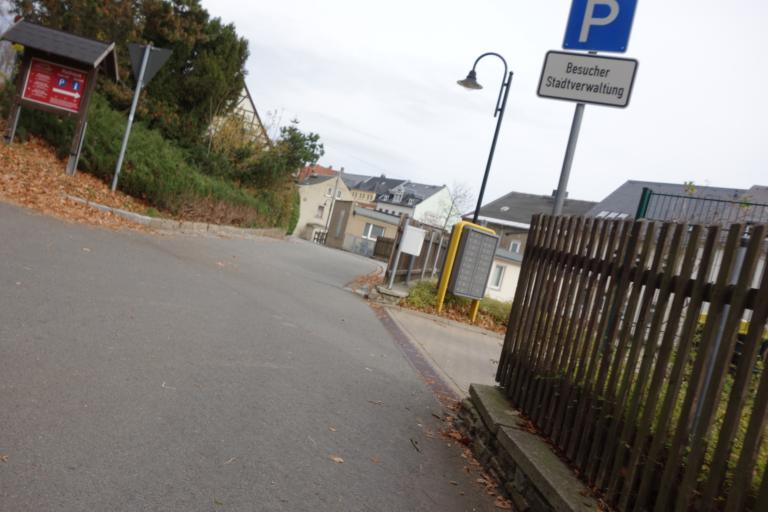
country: DE
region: Saxony
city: Augustusburg
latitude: 50.8105
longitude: 13.1006
